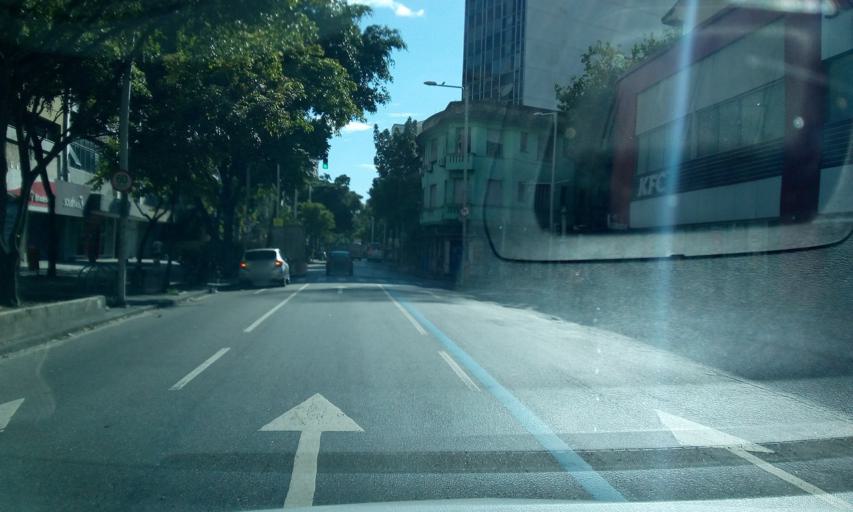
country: BR
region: Rio de Janeiro
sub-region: Rio De Janeiro
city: Rio de Janeiro
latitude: -22.9524
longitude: -43.1871
